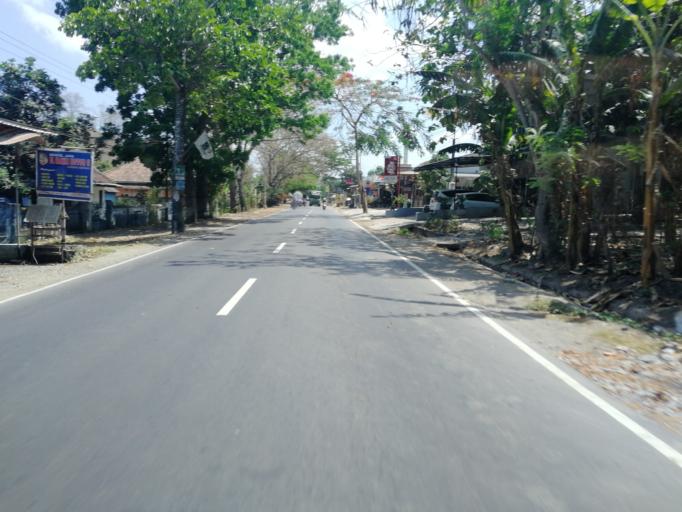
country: ID
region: West Nusa Tenggara
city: Jelateng Timur
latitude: -8.7164
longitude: 116.0744
